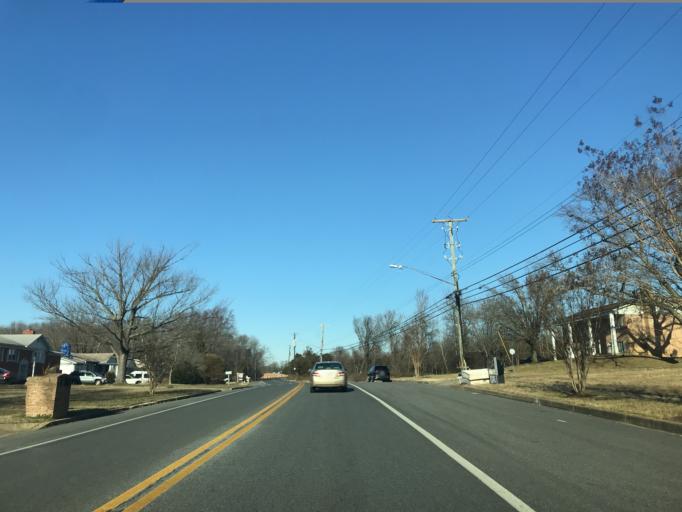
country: US
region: Maryland
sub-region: Prince George's County
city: Friendly
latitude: 38.7299
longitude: -76.9479
